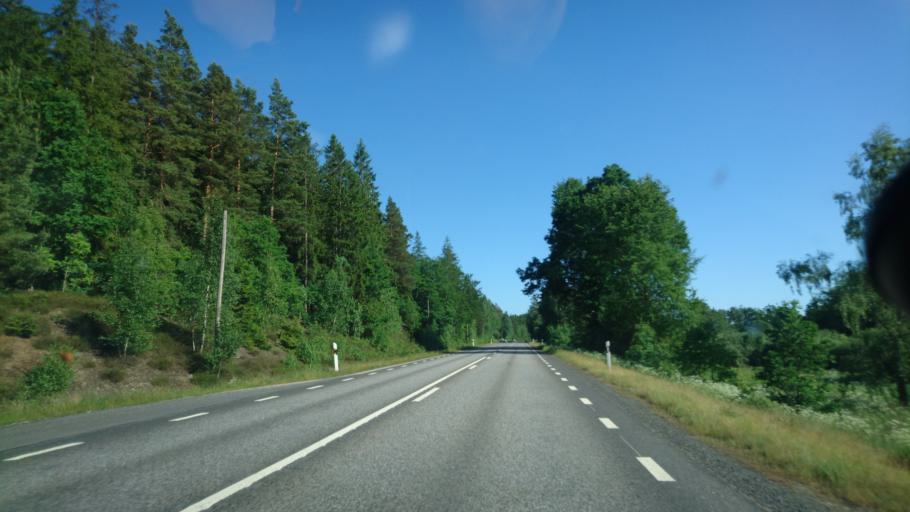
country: SE
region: Blekinge
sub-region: Olofstroms Kommun
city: Olofstroem
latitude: 56.3424
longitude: 14.4912
